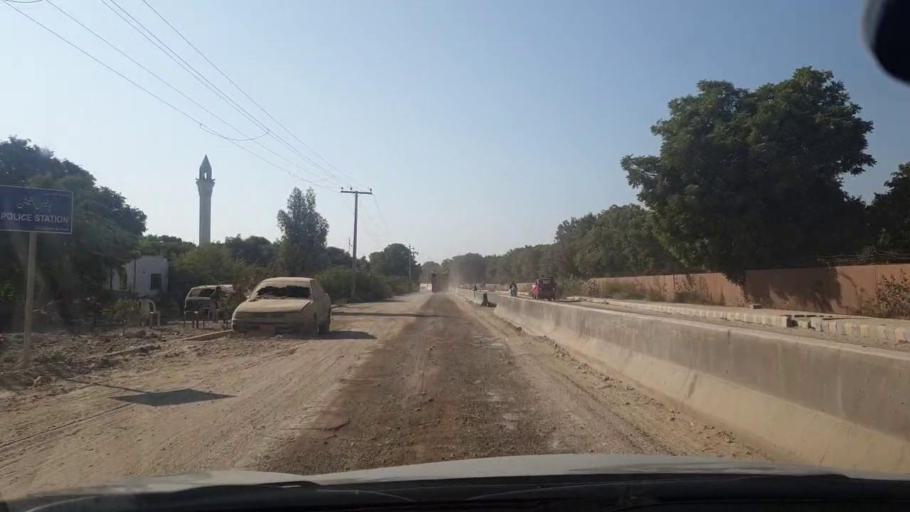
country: PK
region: Sindh
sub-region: Karachi District
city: Karachi
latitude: 25.0887
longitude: 67.0129
